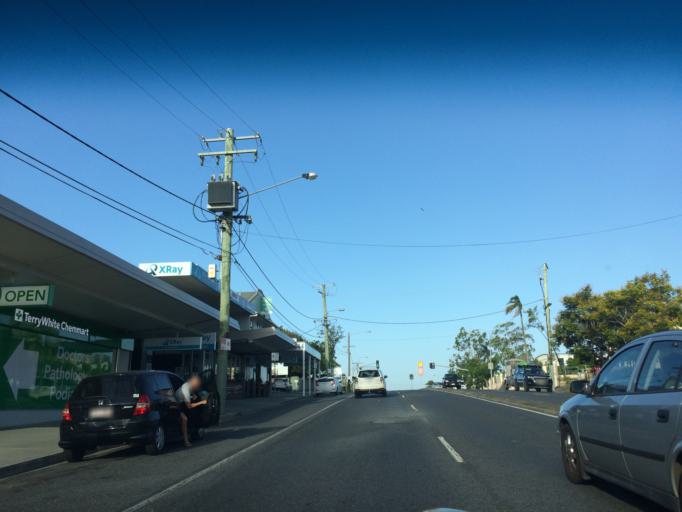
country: AU
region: Queensland
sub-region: Brisbane
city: Camp Hill
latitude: -27.4942
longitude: 153.0599
